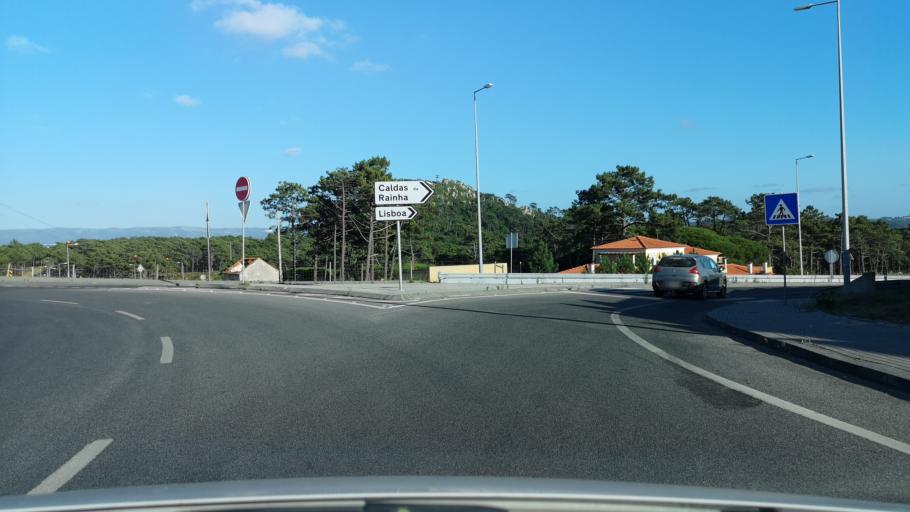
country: PT
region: Leiria
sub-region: Nazare
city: Nazare
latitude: 39.5983
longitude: -9.0588
